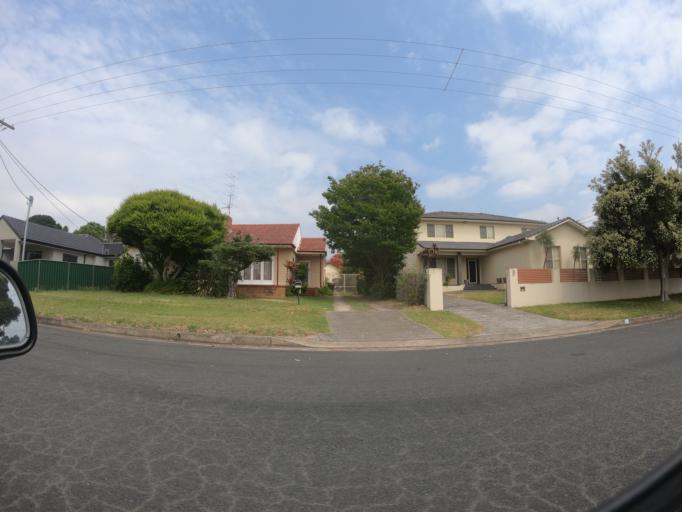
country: AU
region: New South Wales
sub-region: Wollongong
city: Corrimal
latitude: -34.3835
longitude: 150.8938
